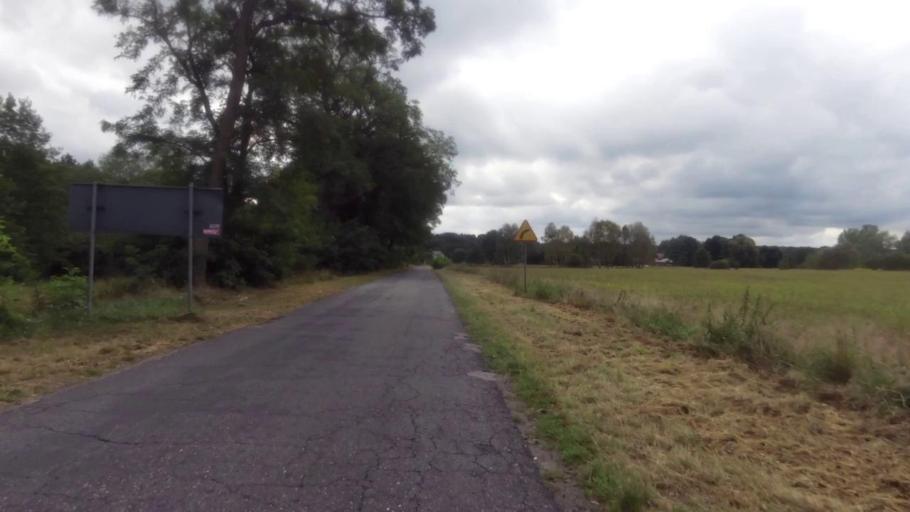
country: PL
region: West Pomeranian Voivodeship
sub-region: Powiat mysliborski
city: Boleszkowice
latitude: 52.6838
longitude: 14.6237
